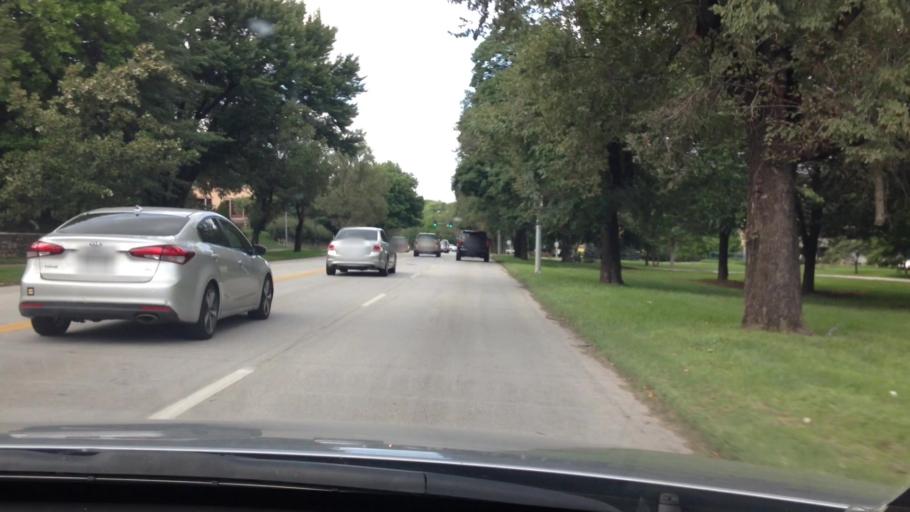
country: US
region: Kansas
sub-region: Johnson County
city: Mission Hills
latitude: 39.0259
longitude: -94.5854
